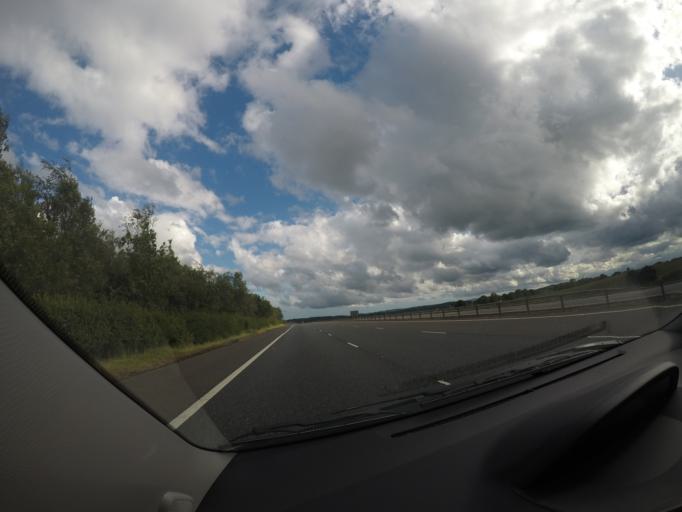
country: GB
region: Scotland
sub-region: Dumfries and Galloway
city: Lochmaben
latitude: 55.2020
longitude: -3.4114
